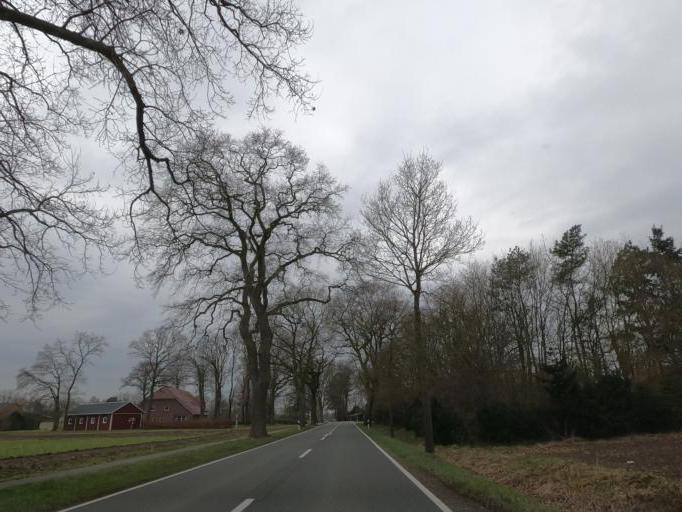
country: DE
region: Lower Saxony
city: Friesoythe
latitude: 52.9740
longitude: 7.8131
